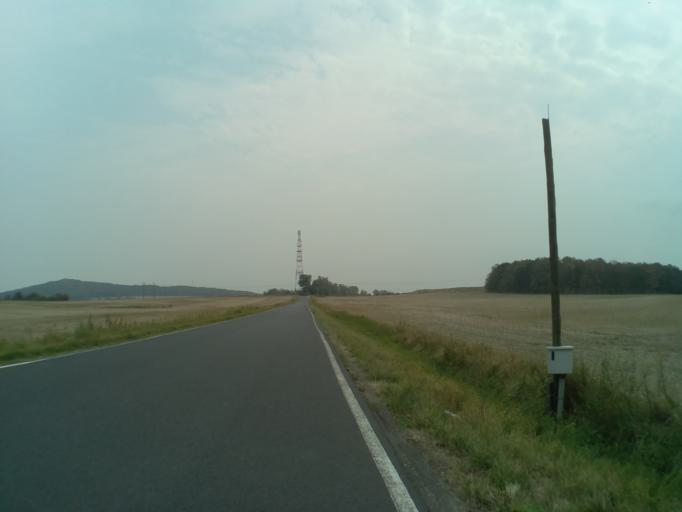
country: PL
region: Lower Silesian Voivodeship
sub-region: Powiat swidnicki
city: Strzegom
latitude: 50.9734
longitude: 16.3029
